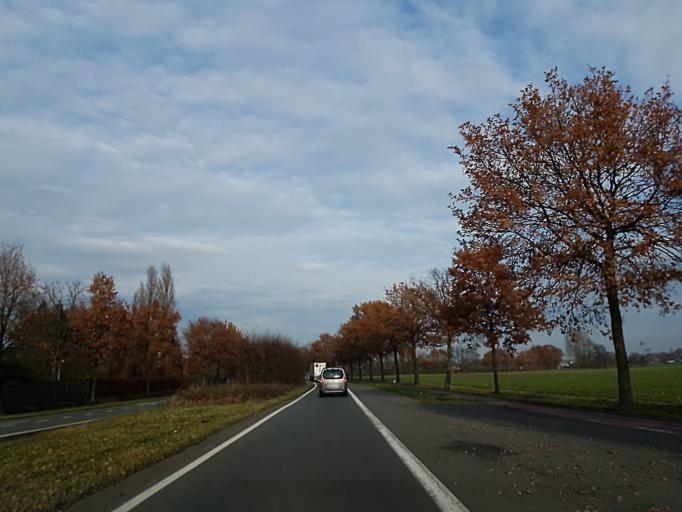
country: BE
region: Flanders
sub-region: Provincie Antwerpen
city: Essen
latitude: 51.4612
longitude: 4.4755
